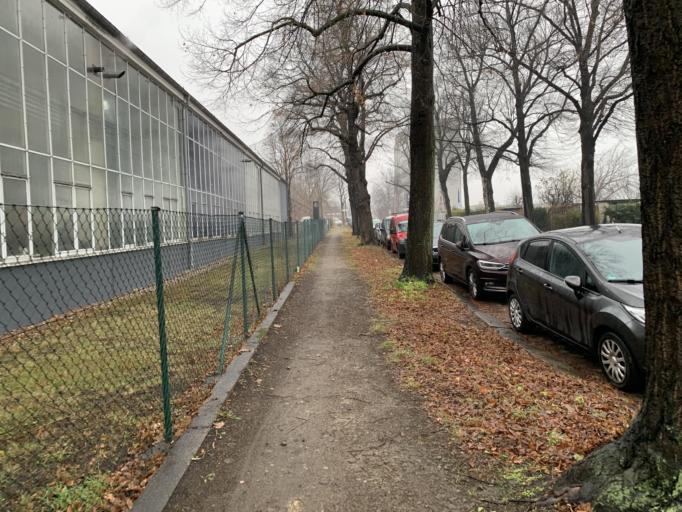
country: DE
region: Saxony
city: Dresden
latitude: 51.0281
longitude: 13.7861
